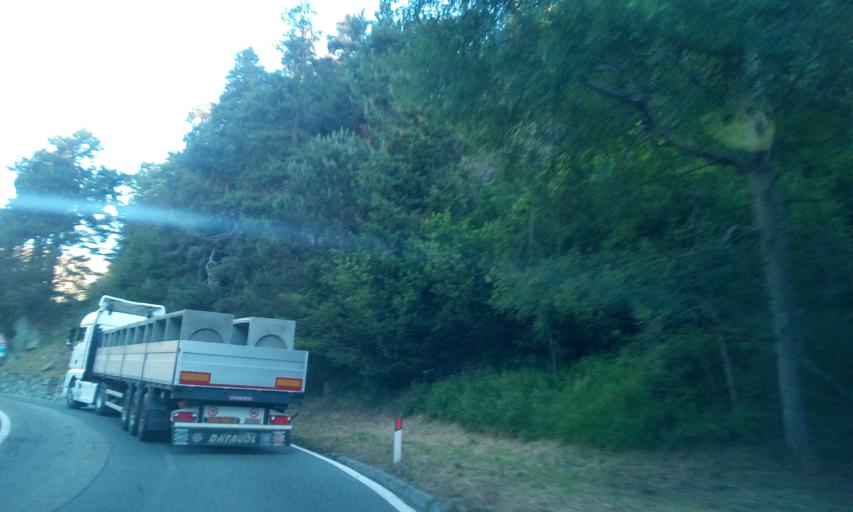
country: IT
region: Aosta Valley
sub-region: Valle d'Aosta
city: Antagnod
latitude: 45.7879
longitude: 7.7015
